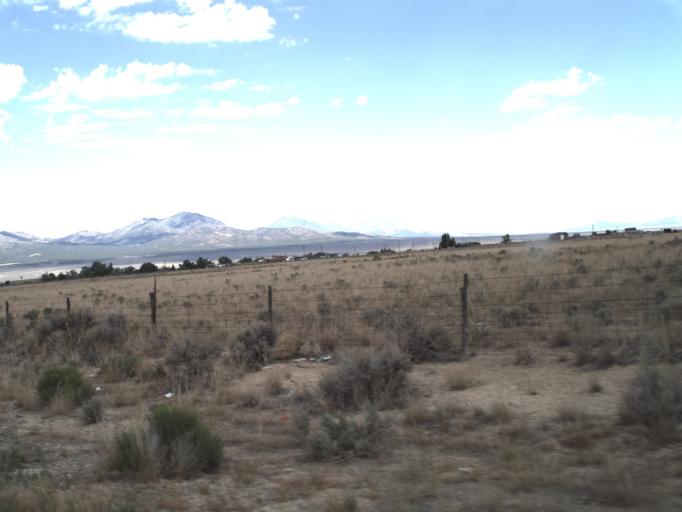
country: US
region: Utah
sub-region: Tooele County
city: Tooele
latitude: 40.0859
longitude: -112.4245
